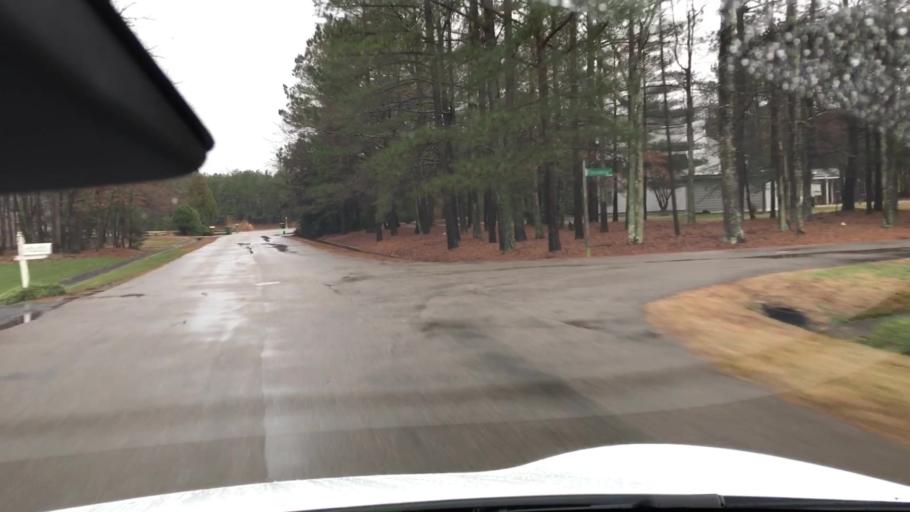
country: US
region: Virginia
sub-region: Chesterfield County
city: Bon Air
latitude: 37.5329
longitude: -77.5980
